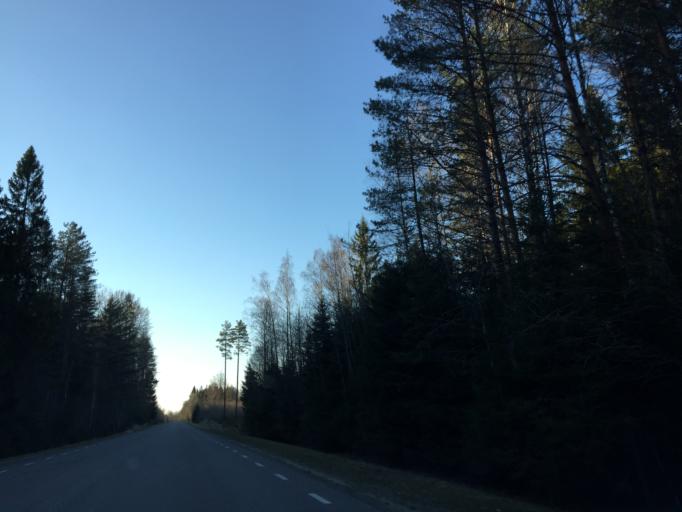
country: EE
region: Ida-Virumaa
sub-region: Toila vald
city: Voka
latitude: 59.1702
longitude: 27.5757
